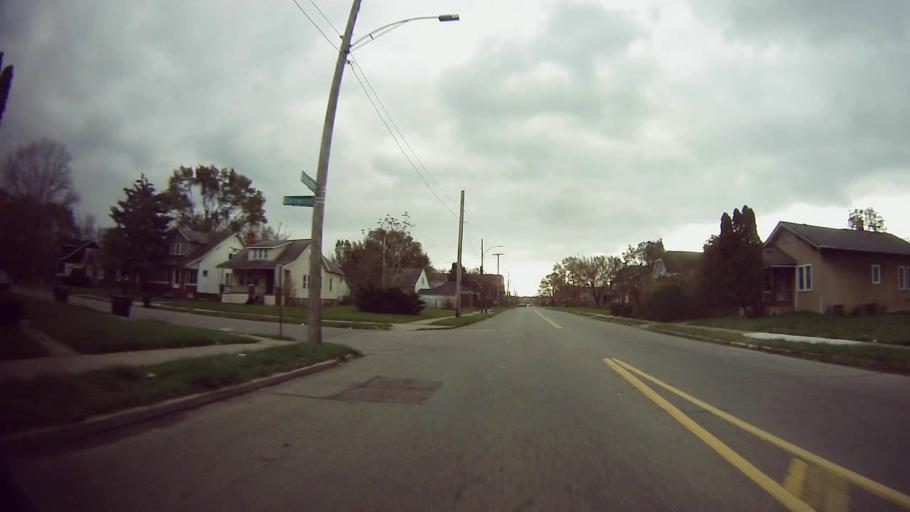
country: US
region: Michigan
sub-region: Macomb County
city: Eastpointe
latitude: 42.4307
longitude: -82.9849
